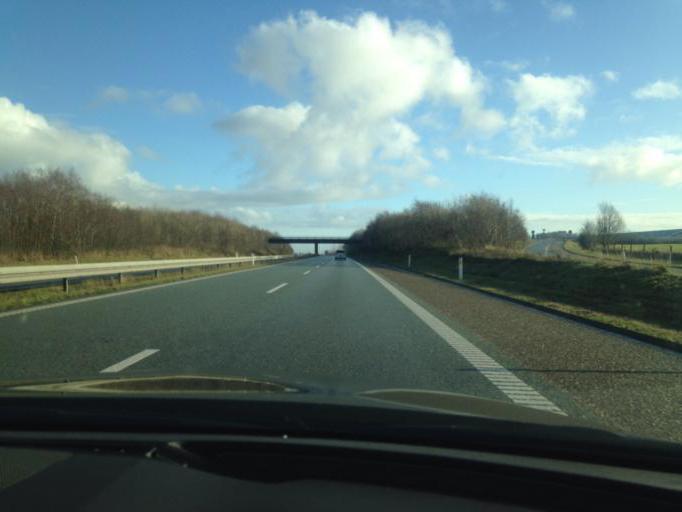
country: DK
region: South Denmark
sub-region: Vejen Kommune
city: Brorup
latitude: 55.5046
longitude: 9.0176
